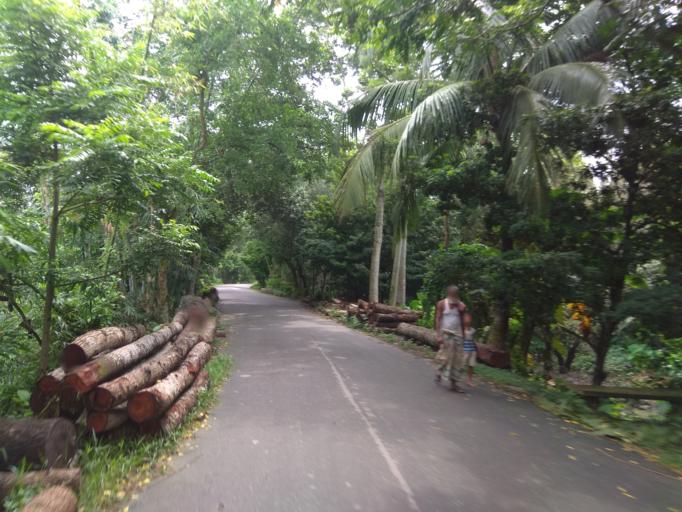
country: BD
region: Dhaka
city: Dohar
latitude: 23.4427
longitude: 90.0684
